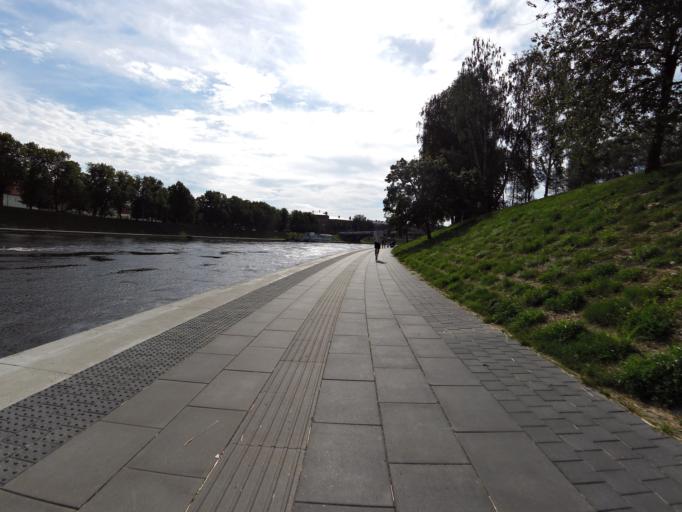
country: LT
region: Vilnius County
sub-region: Vilnius
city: Vilnius
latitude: 54.6895
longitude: 25.2921
